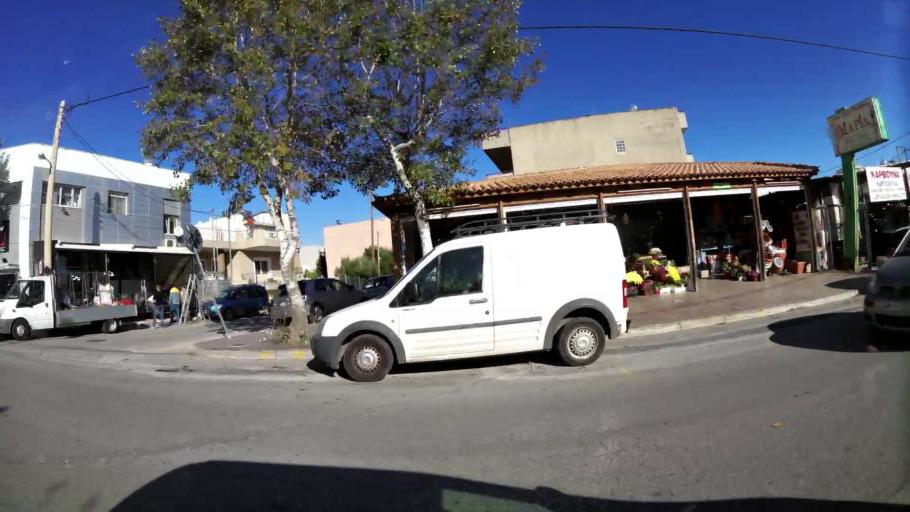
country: GR
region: Attica
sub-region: Nomarchia Anatolikis Attikis
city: Acharnes
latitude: 38.0917
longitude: 23.7261
